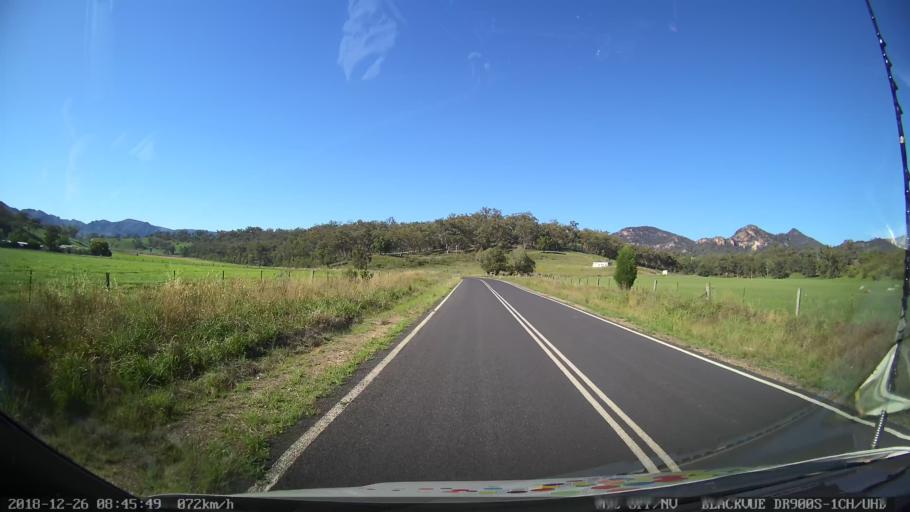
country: AU
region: New South Wales
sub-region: Mid-Western Regional
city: Kandos
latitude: -32.5295
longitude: 150.0862
